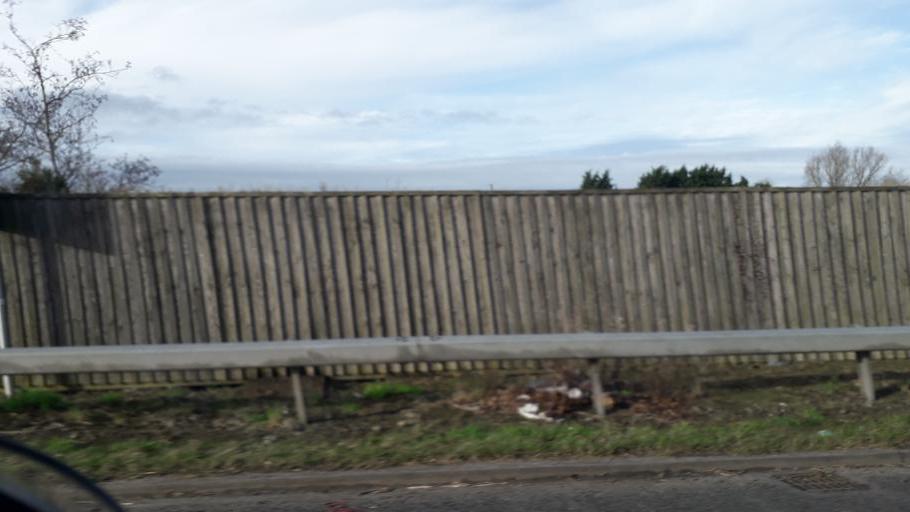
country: IE
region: Leinster
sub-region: Lu
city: Dromiskin
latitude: 53.9432
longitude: -6.4182
